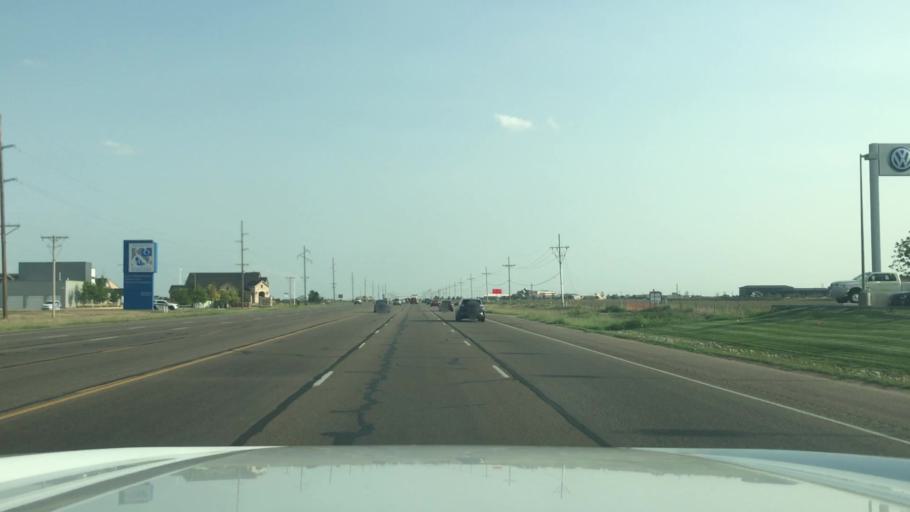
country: US
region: Texas
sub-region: Potter County
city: Amarillo
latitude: 35.1578
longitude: -101.9383
